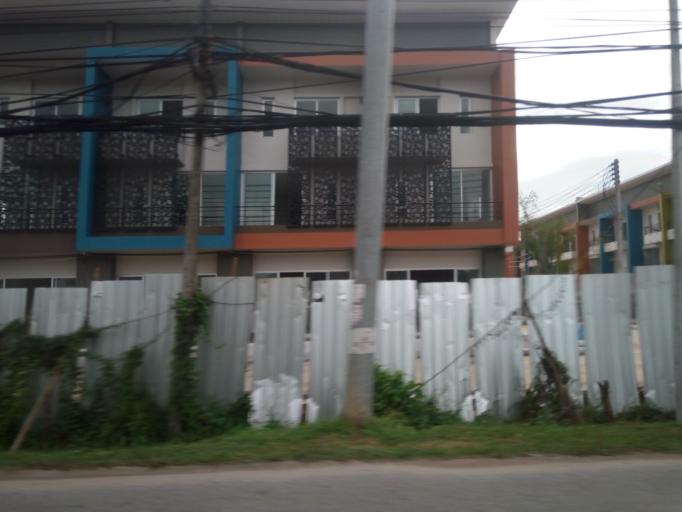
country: TH
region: Phuket
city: Thalang
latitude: 7.9998
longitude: 98.3482
